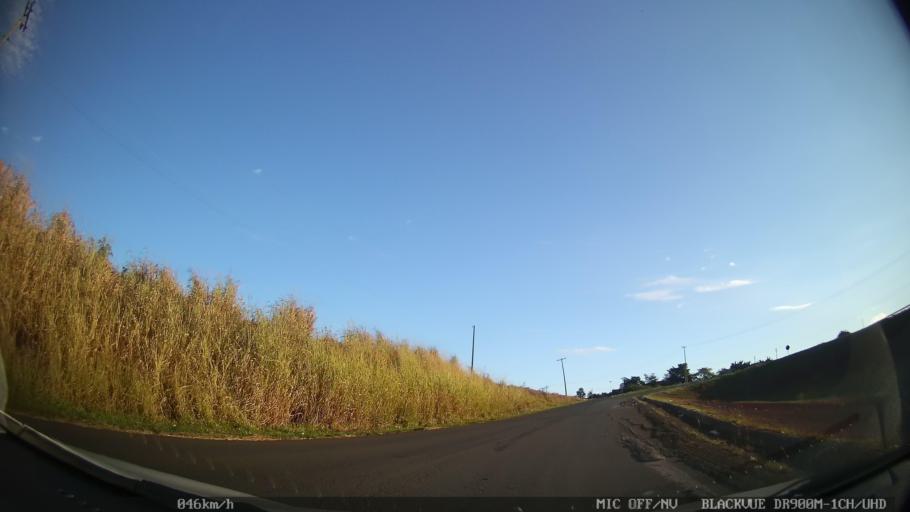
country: BR
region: Sao Paulo
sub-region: Piracicaba
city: Piracicaba
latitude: -22.7247
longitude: -47.5840
